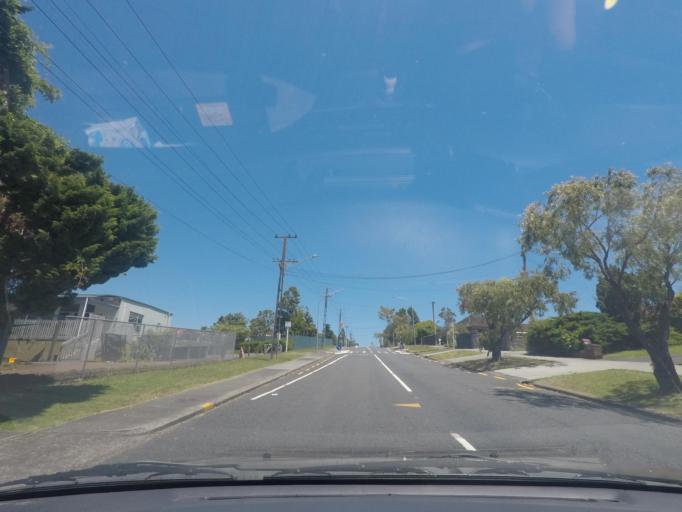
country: NZ
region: Auckland
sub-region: Auckland
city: Waitakere
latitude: -36.9172
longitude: 174.7149
